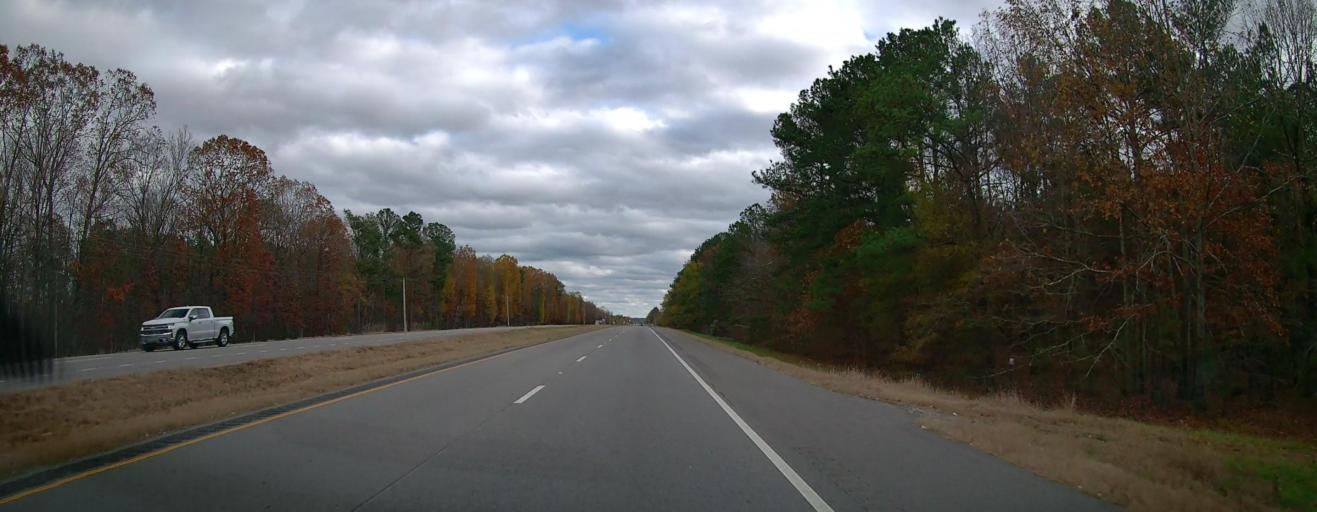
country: US
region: Alabama
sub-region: Lawrence County
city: Town Creek
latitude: 34.6582
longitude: -87.5380
